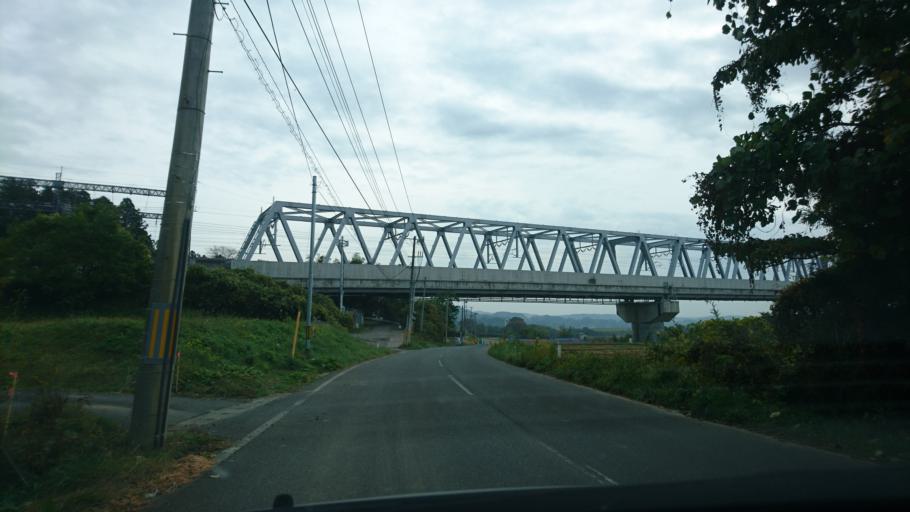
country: JP
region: Iwate
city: Ichinoseki
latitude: 38.9768
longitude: 141.1557
